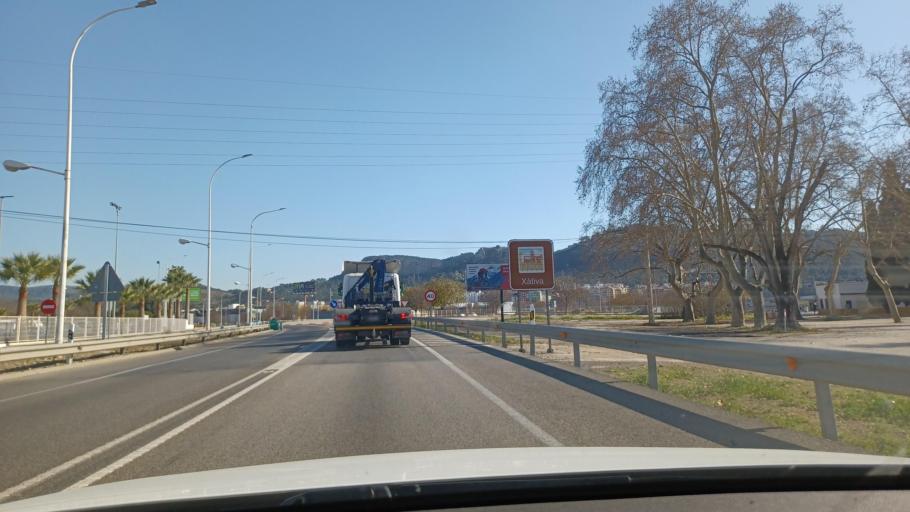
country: ES
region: Valencia
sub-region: Provincia de Valencia
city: Xativa
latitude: 38.9998
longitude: -0.5271
